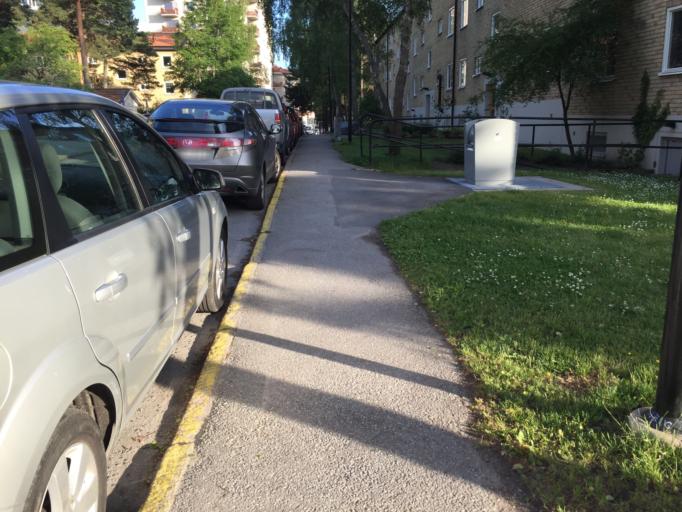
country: SE
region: Stockholm
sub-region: Stockholms Kommun
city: Bromma
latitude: 59.3442
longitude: 17.8843
